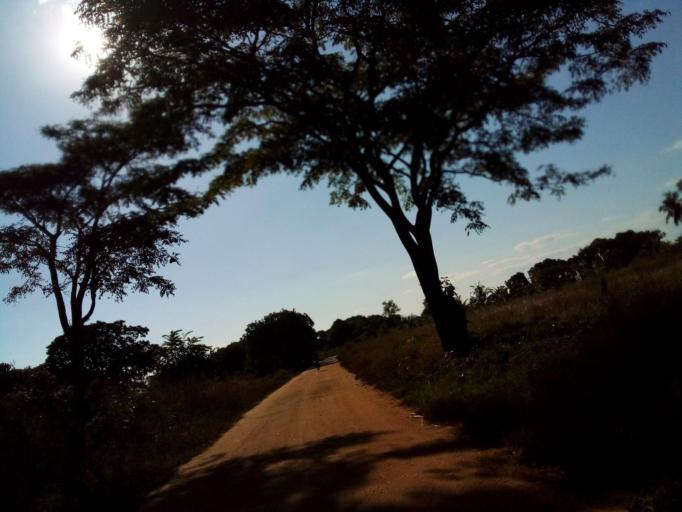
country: MZ
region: Zambezia
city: Quelimane
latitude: -17.5333
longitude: 36.6210
